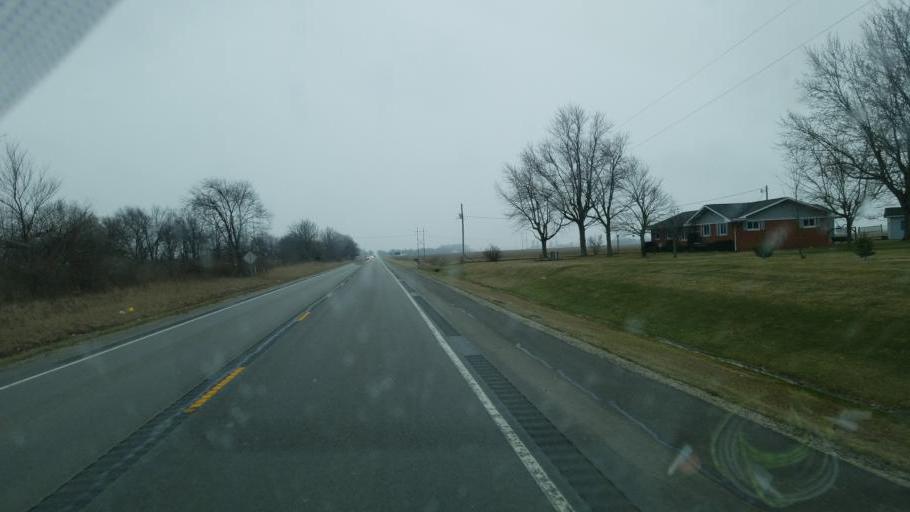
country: US
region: Indiana
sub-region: Wabash County
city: Wabash
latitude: 40.7647
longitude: -85.8165
